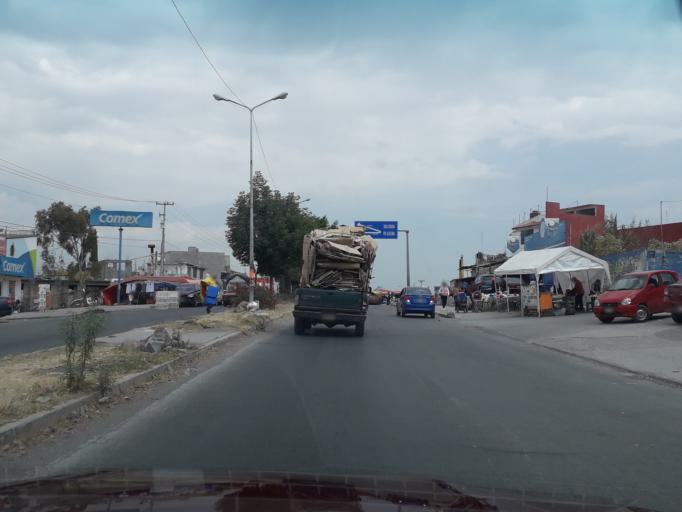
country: MX
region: Puebla
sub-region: Puebla
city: El Capulo (La Quebradora)
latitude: 18.9632
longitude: -98.2669
